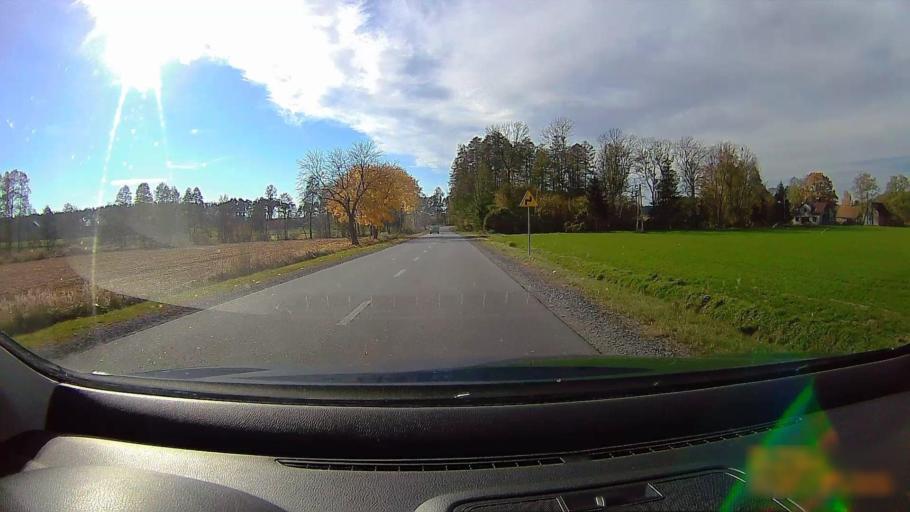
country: PL
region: Greater Poland Voivodeship
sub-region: Powiat ostrzeszowski
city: Doruchow
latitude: 51.3879
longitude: 18.0505
